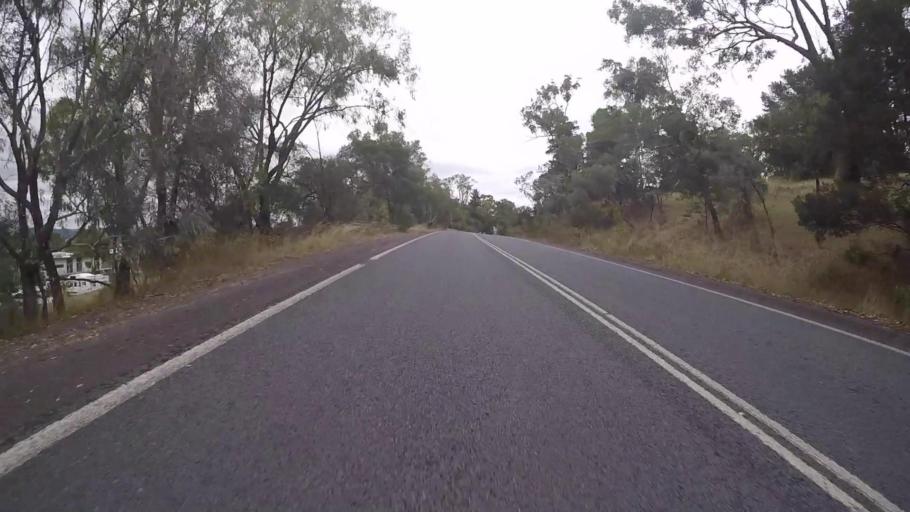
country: AU
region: Australian Capital Territory
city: Canberra
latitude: -35.2936
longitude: 149.1611
